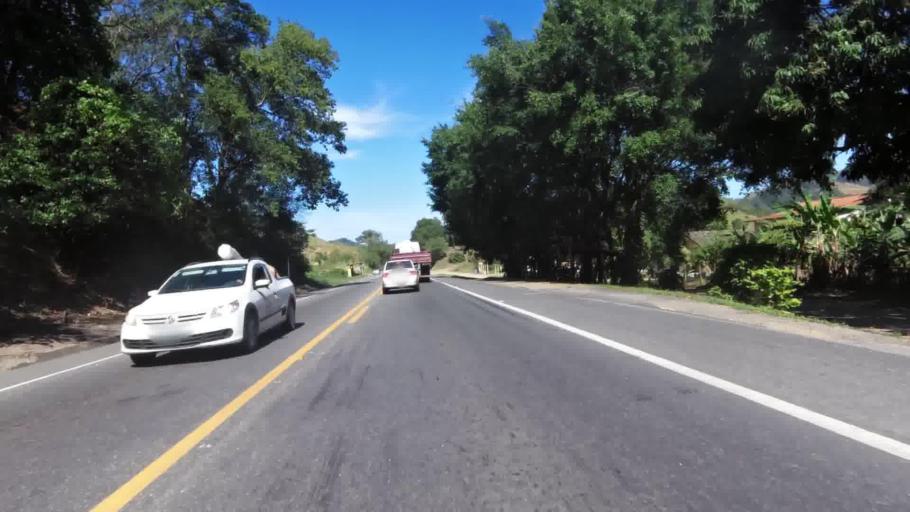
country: BR
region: Espirito Santo
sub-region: Iconha
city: Iconha
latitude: -20.8019
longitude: -40.8280
